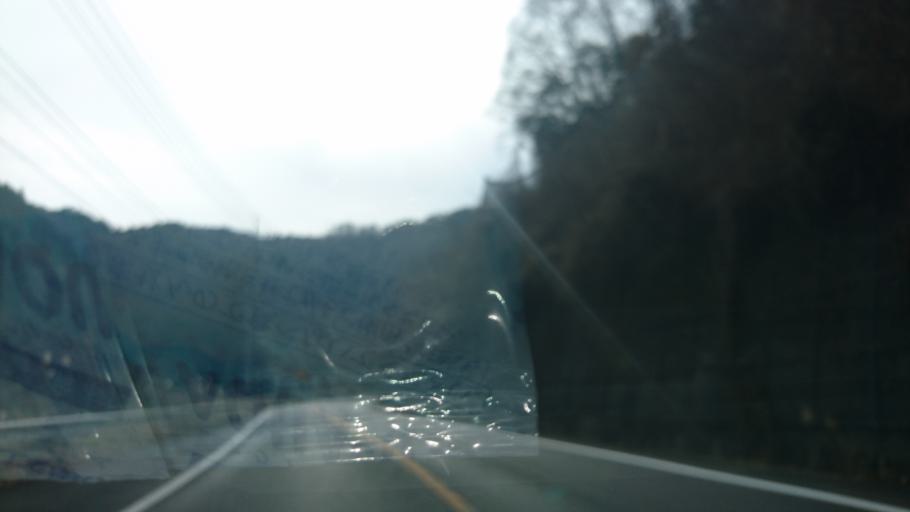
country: JP
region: Okayama
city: Takahashi
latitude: 34.8237
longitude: 133.6617
